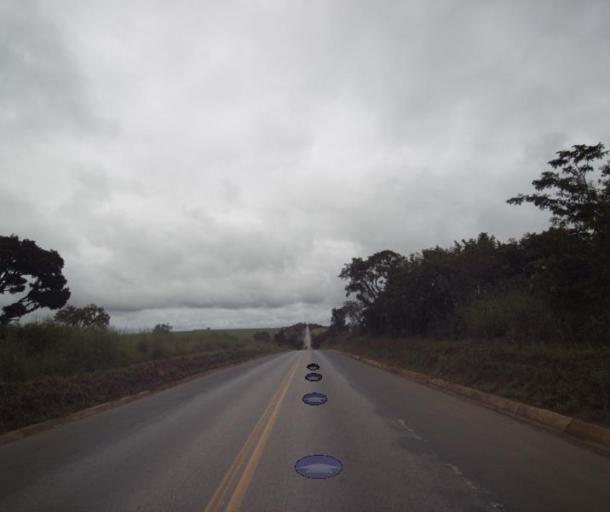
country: BR
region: Goias
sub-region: Uruacu
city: Uruacu
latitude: -14.6095
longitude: -49.1678
